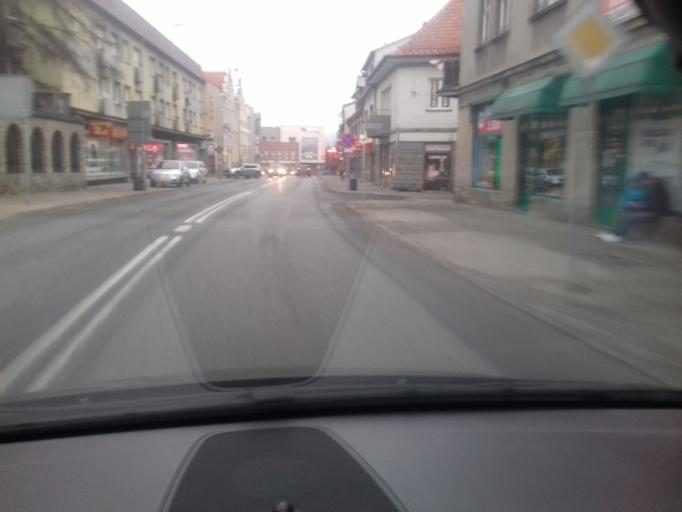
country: PL
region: Lesser Poland Voivodeship
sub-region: Powiat limanowski
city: Limanowa
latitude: 49.7067
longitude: 20.4211
